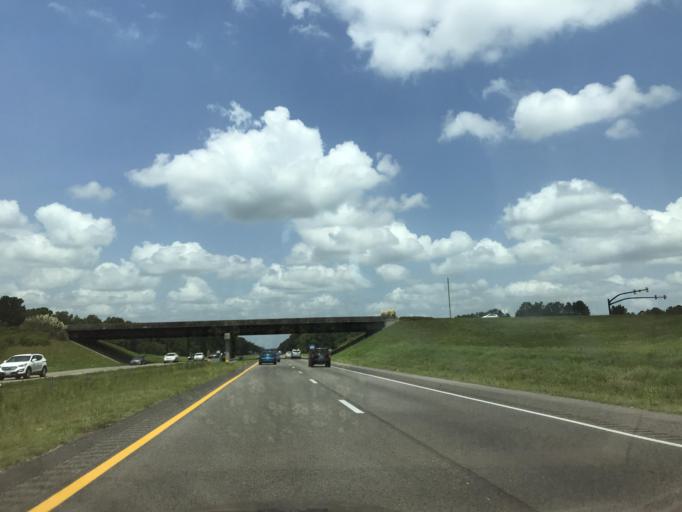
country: US
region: North Carolina
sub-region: Pender County
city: Rocky Point
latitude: 34.4399
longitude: -77.8739
